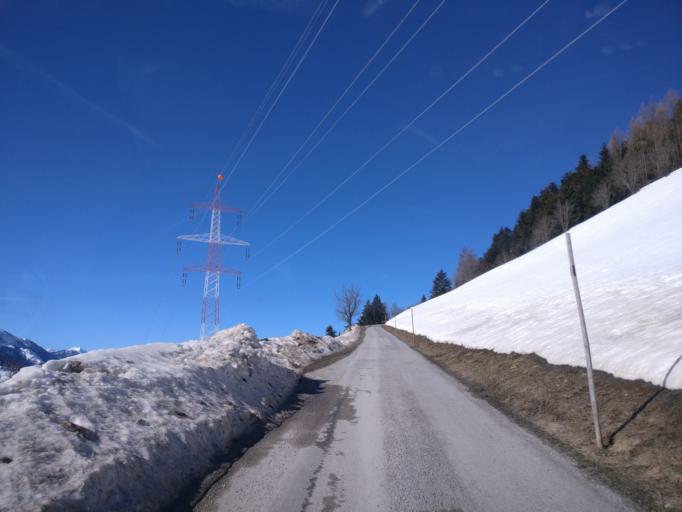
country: AT
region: Salzburg
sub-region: Politischer Bezirk Sankt Johann im Pongau
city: Sankt Johann im Pongau
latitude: 47.3362
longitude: 13.2341
